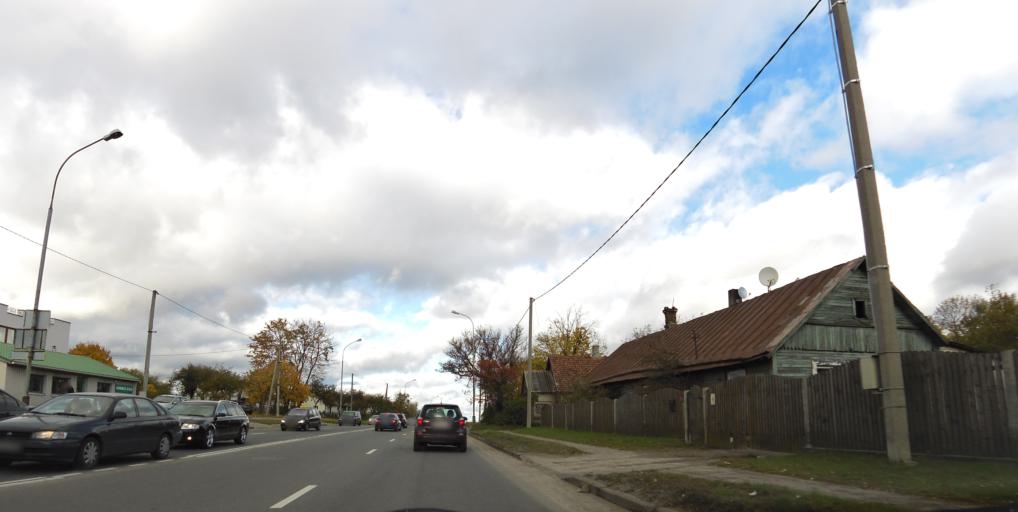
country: LT
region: Vilnius County
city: Rasos
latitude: 54.6553
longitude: 25.3030
